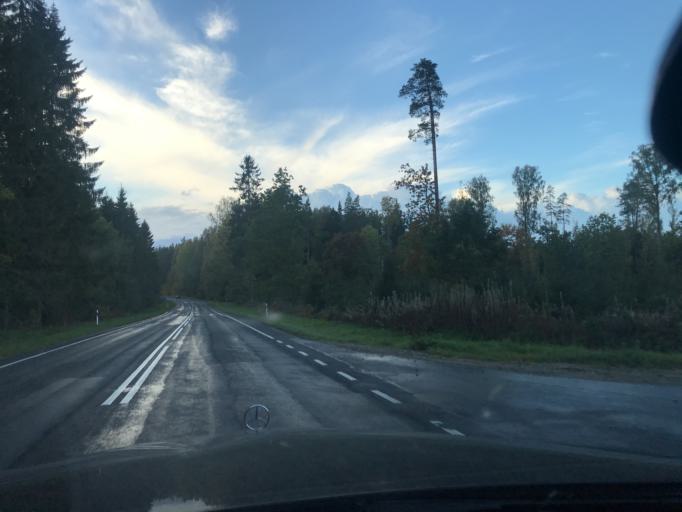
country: EE
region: Vorumaa
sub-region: Antsla vald
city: Vana-Antsla
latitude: 57.8787
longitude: 26.5803
